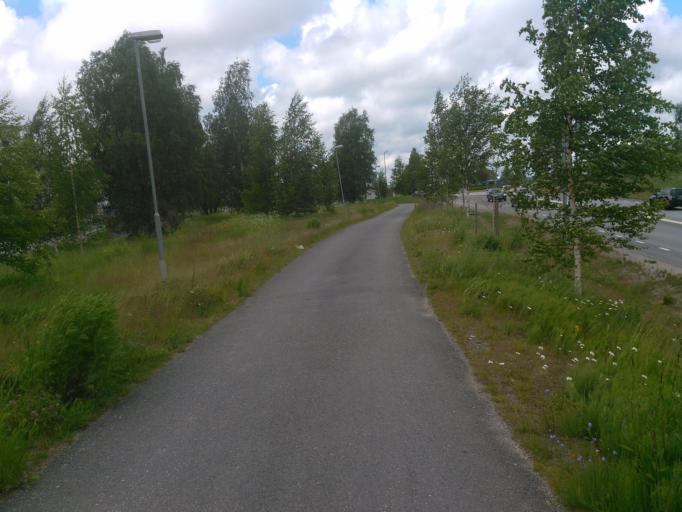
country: SE
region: Vaesterbotten
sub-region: Umea Kommun
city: Umea
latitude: 63.8402
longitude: 20.2426
